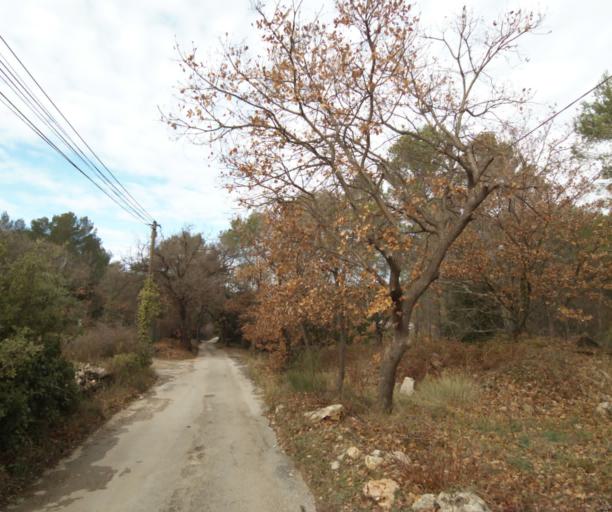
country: FR
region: Provence-Alpes-Cote d'Azur
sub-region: Departement du Var
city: Trans-en-Provence
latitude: 43.5154
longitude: 6.4935
